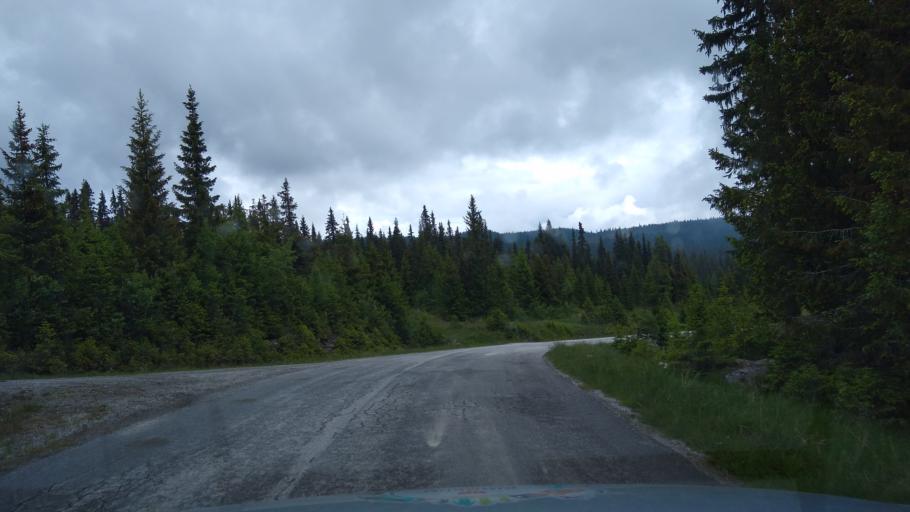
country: NO
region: Oppland
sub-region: Ringebu
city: Ringebu
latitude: 61.4888
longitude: 10.1128
